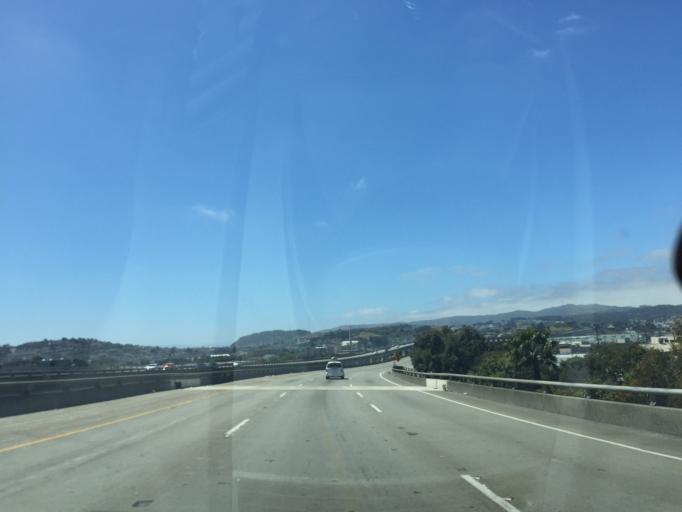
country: US
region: California
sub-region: San Francisco County
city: San Francisco
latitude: 37.7523
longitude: -122.3917
